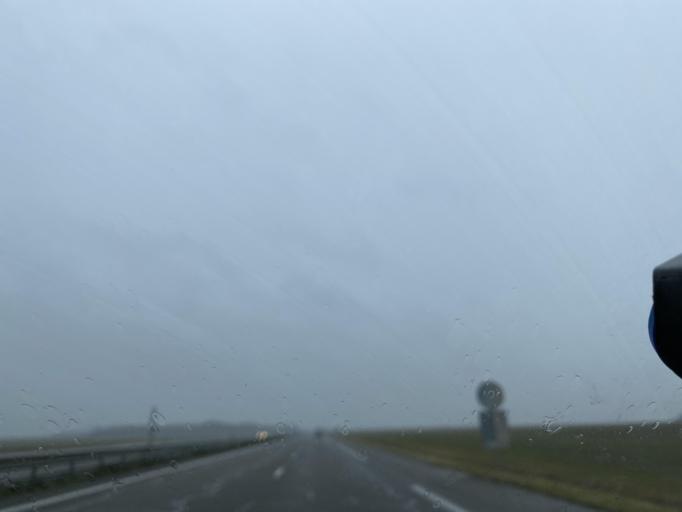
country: FR
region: Centre
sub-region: Departement d'Eure-et-Loir
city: Villemeux-sur-Eure
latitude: 48.6225
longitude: 1.4160
